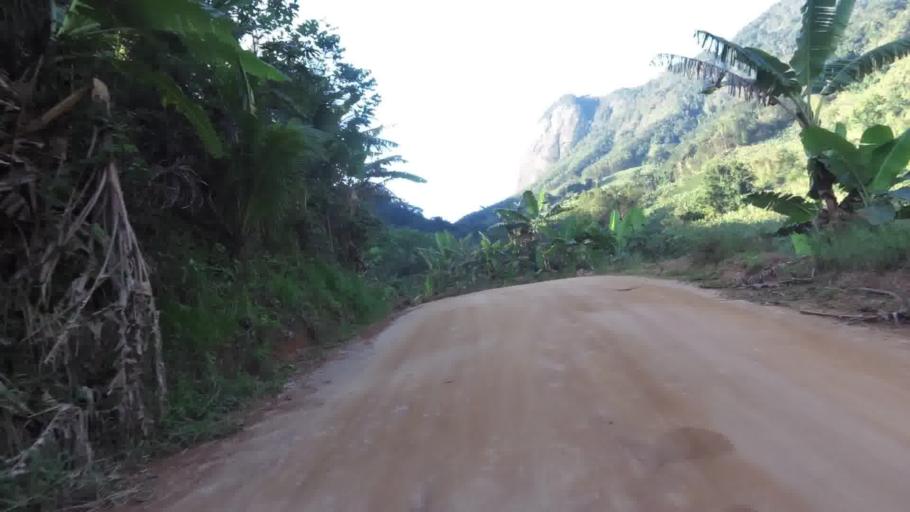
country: BR
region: Espirito Santo
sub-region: Alfredo Chaves
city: Alfredo Chaves
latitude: -20.5735
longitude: -40.6970
